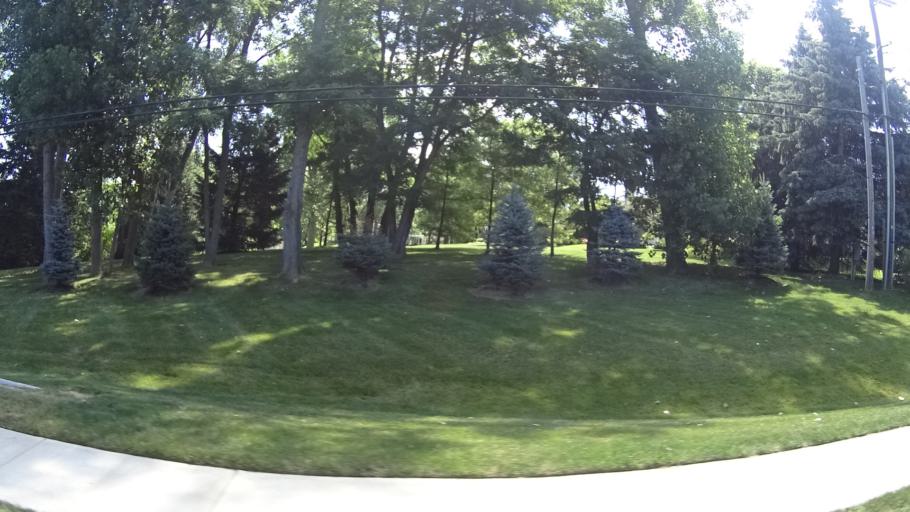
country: US
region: Ohio
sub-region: Erie County
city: Huron
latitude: 41.3775
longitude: -82.5662
